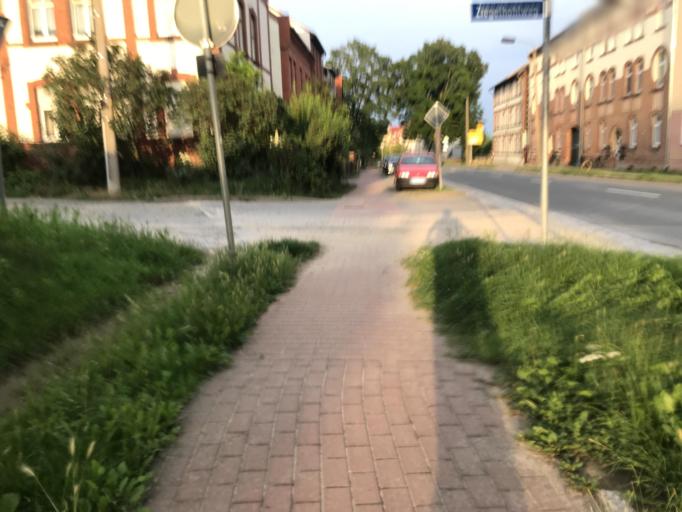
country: DE
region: Saxony-Anhalt
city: Quedlinburg
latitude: 51.7965
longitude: 11.1414
